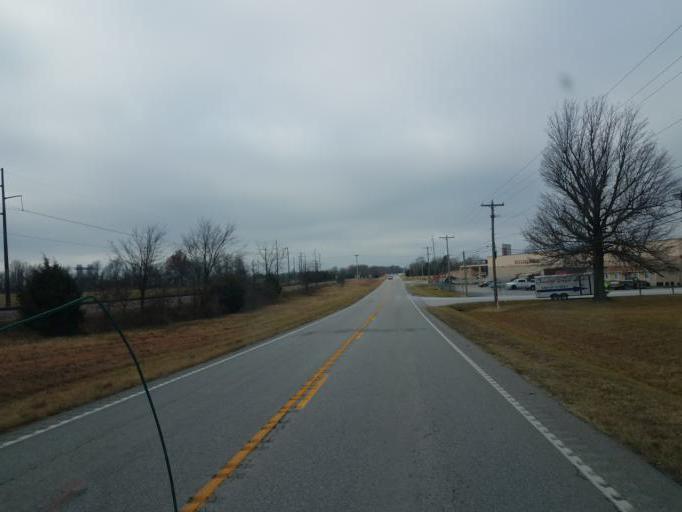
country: US
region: Missouri
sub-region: Greene County
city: Strafford
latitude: 37.2515
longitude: -93.1675
